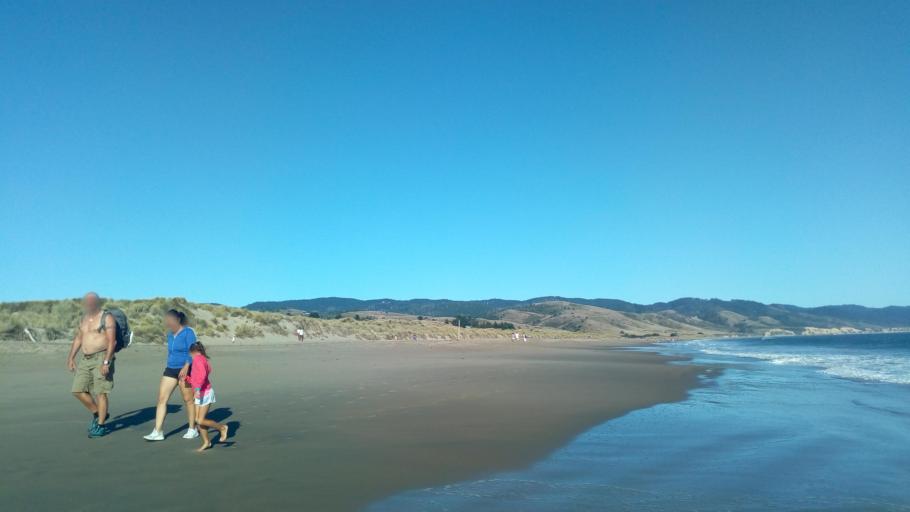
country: US
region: California
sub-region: Marin County
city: Inverness
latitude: 38.0266
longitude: -122.8906
